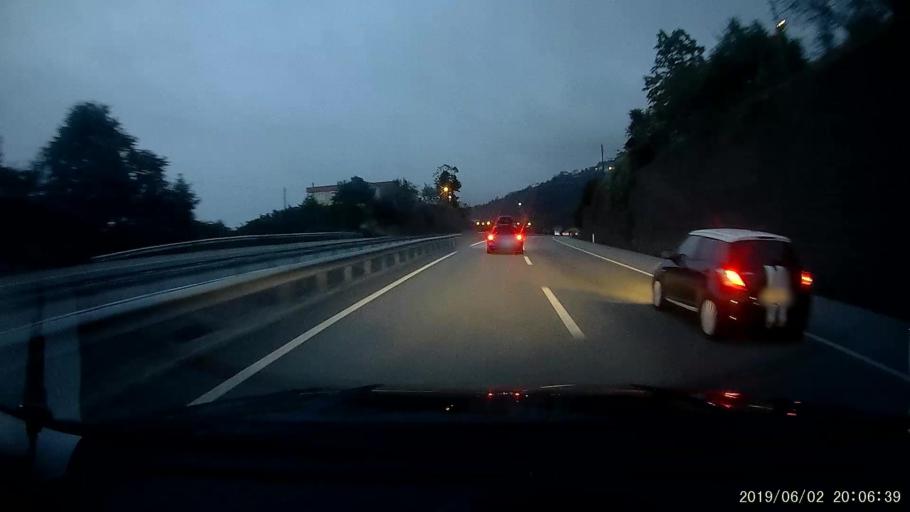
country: TR
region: Giresun
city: Gorele
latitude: 41.0363
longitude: 38.9593
